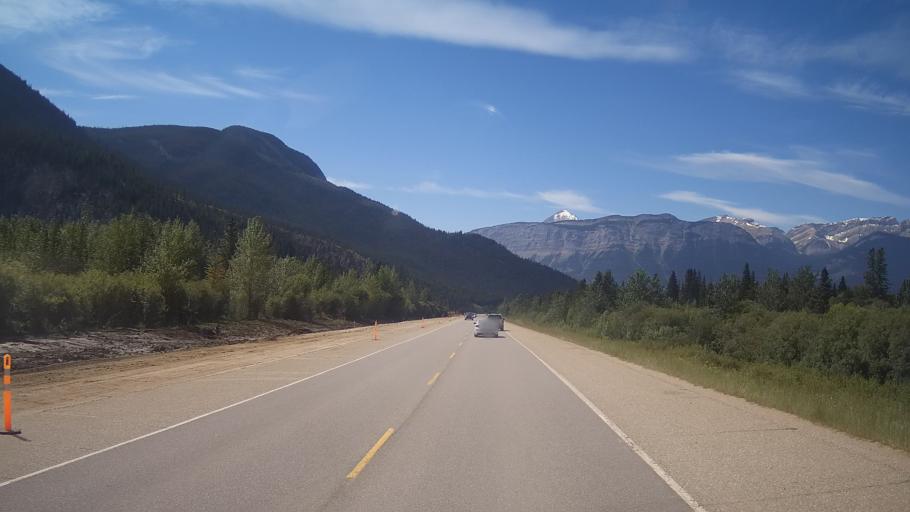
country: CA
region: Alberta
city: Jasper Park Lodge
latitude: 53.0625
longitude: -118.0656
